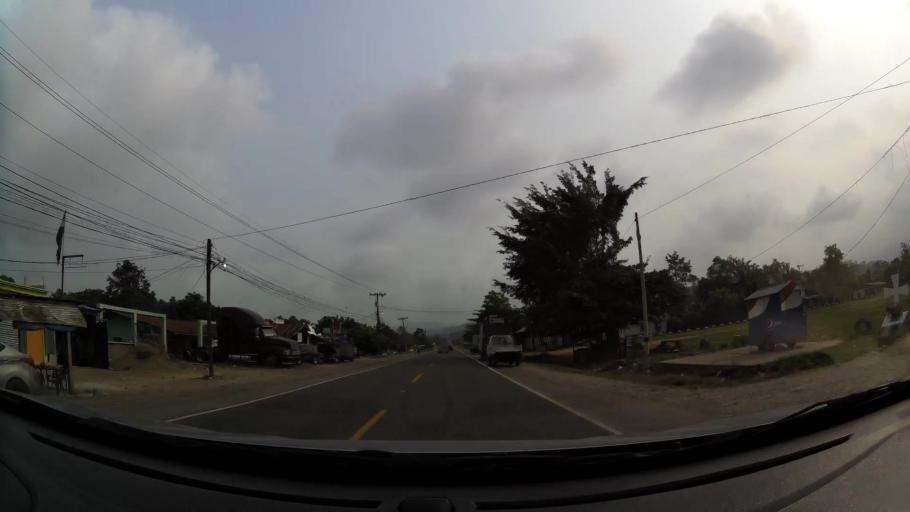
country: HN
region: Yoro
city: Toyos
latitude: 15.5398
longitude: -87.6525
